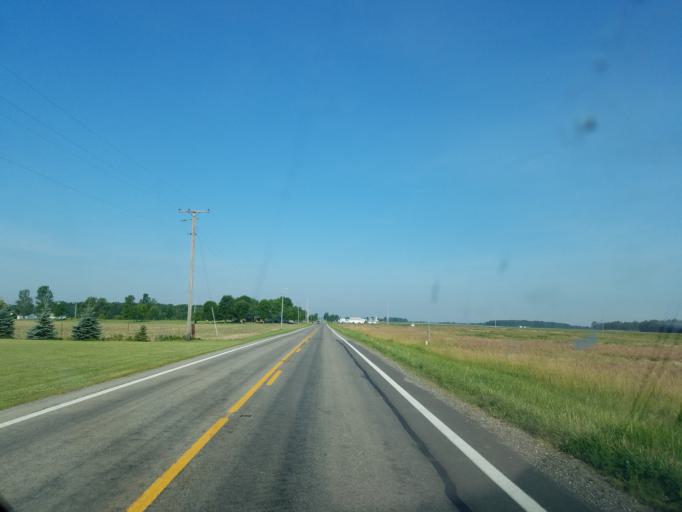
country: US
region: Ohio
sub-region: Hardin County
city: Kenton
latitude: 40.7319
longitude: -83.6480
